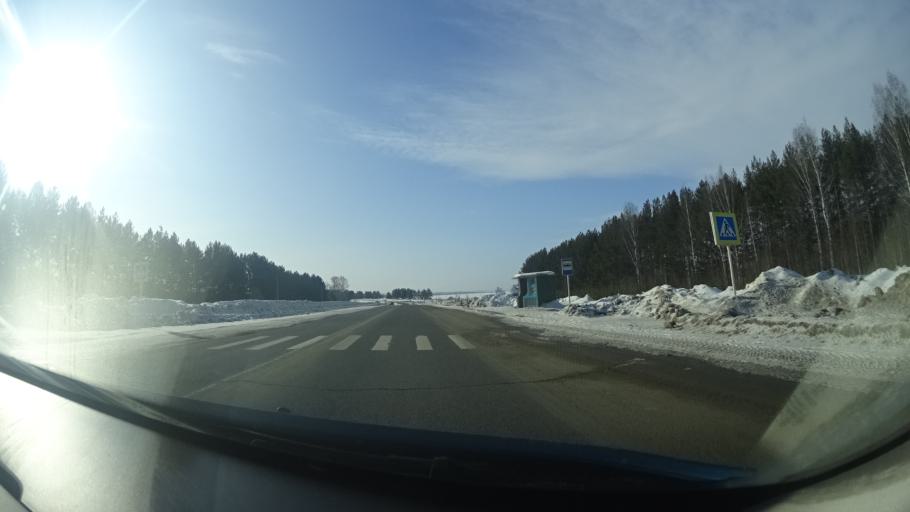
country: RU
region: Perm
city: Kuyeda
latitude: 56.4755
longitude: 55.5897
